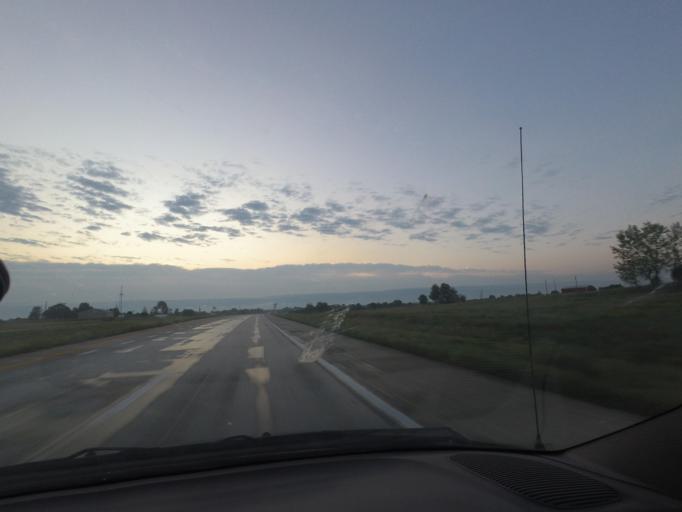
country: US
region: Missouri
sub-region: Macon County
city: Macon
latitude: 39.7581
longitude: -92.6423
